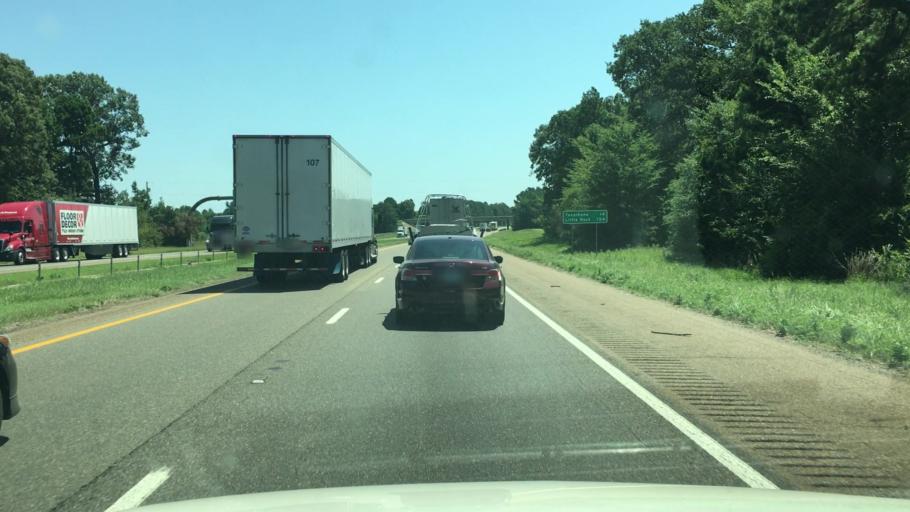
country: US
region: Texas
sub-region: Bowie County
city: Hooks
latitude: 33.4763
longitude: -94.2759
